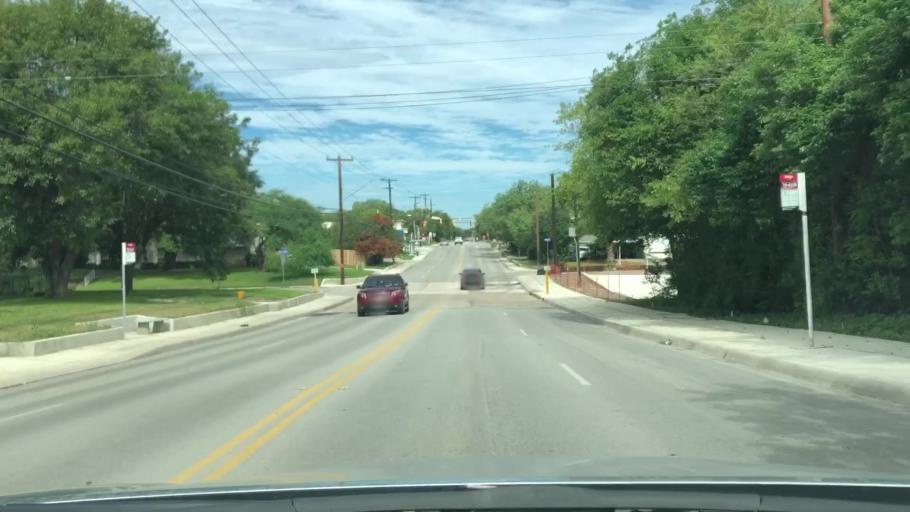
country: US
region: Texas
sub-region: Bexar County
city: Olmos Park
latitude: 29.5027
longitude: -98.4917
